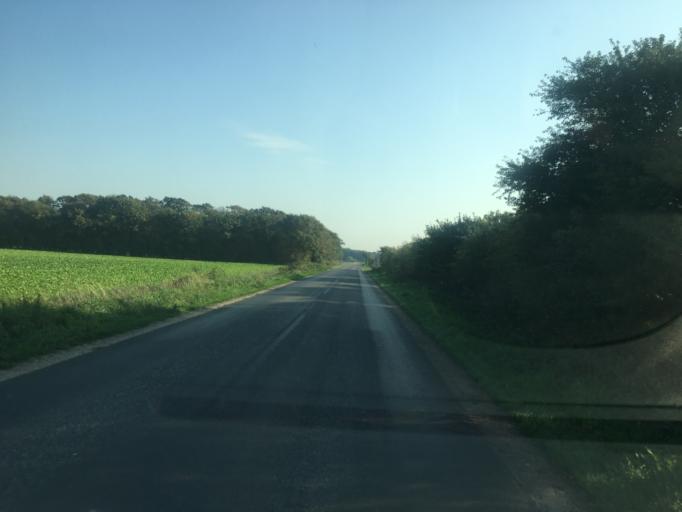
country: DE
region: Schleswig-Holstein
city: Bramstedtlund
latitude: 54.9348
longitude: 9.0674
